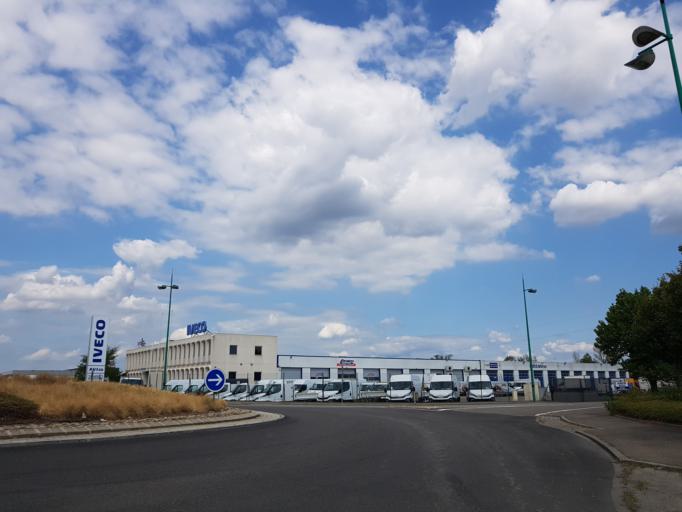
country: FR
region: Alsace
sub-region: Departement du Haut-Rhin
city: Sausheim
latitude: 47.7859
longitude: 7.3882
